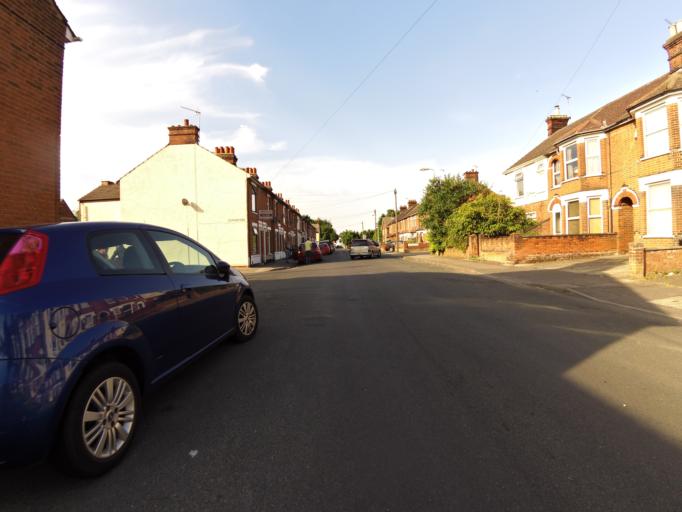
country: GB
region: England
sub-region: Suffolk
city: Ipswich
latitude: 52.0547
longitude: 1.1762
